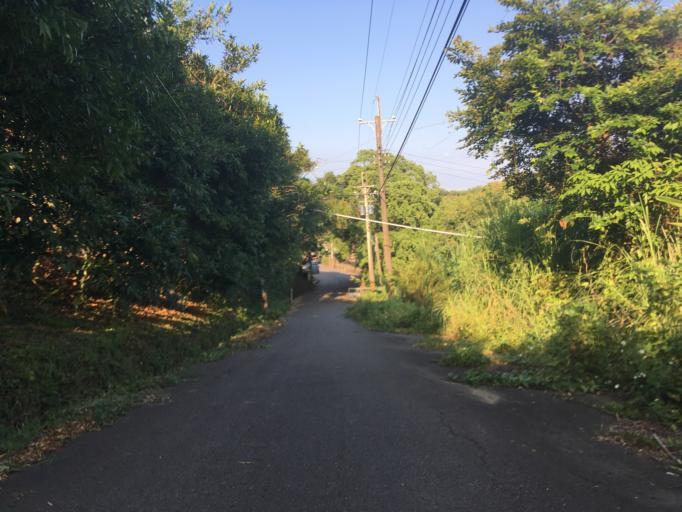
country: TW
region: Taiwan
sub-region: Hsinchu
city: Hsinchu
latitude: 24.7393
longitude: 120.9886
